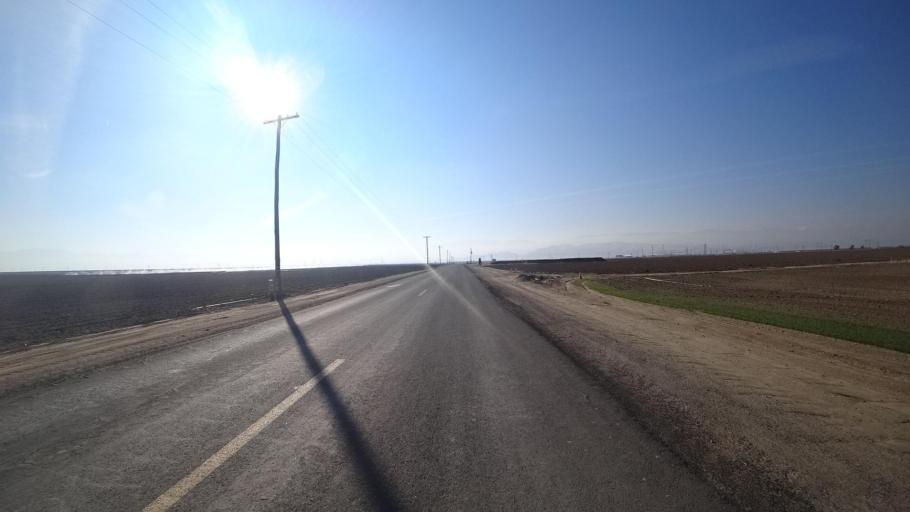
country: US
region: California
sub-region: Kern County
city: Weedpatch
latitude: 35.0987
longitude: -118.9677
